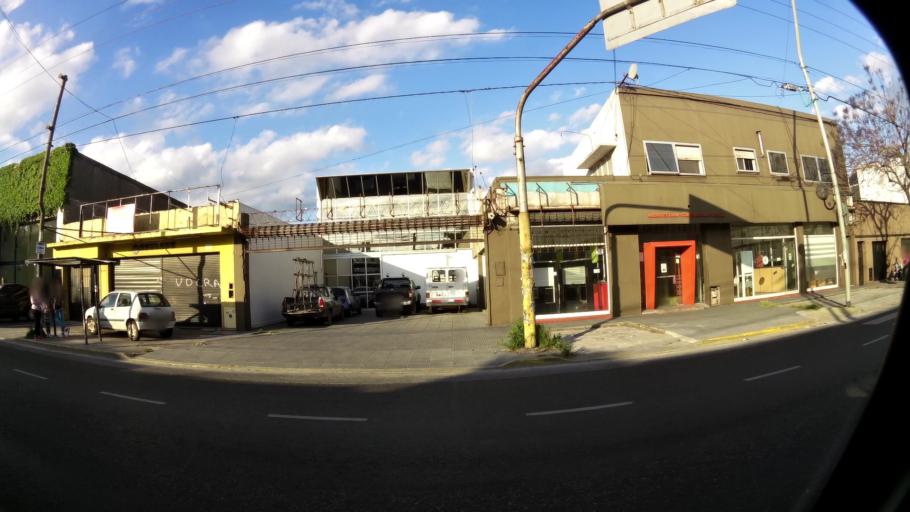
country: AR
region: Buenos Aires
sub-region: Partido de La Plata
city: La Plata
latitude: -34.8962
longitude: -57.9420
